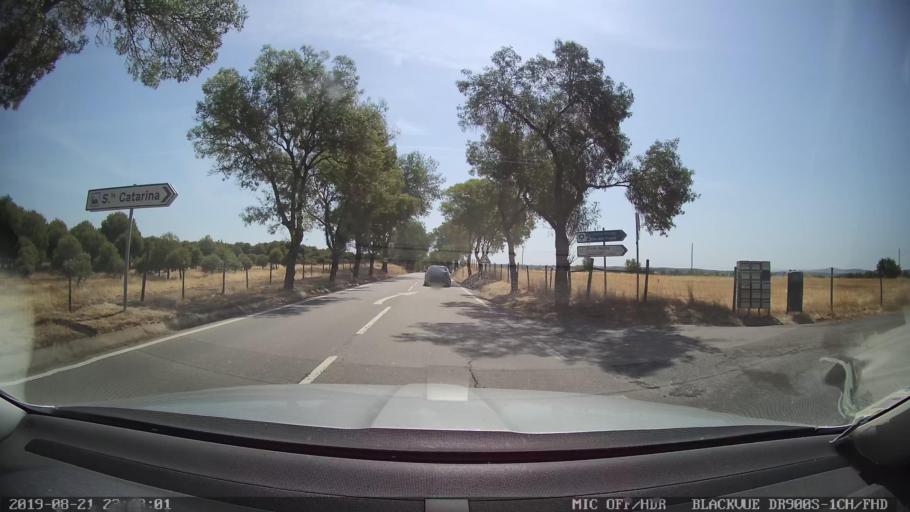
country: PT
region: Castelo Branco
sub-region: Idanha-A-Nova
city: Idanha-a-Nova
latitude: 39.8521
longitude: -7.3026
